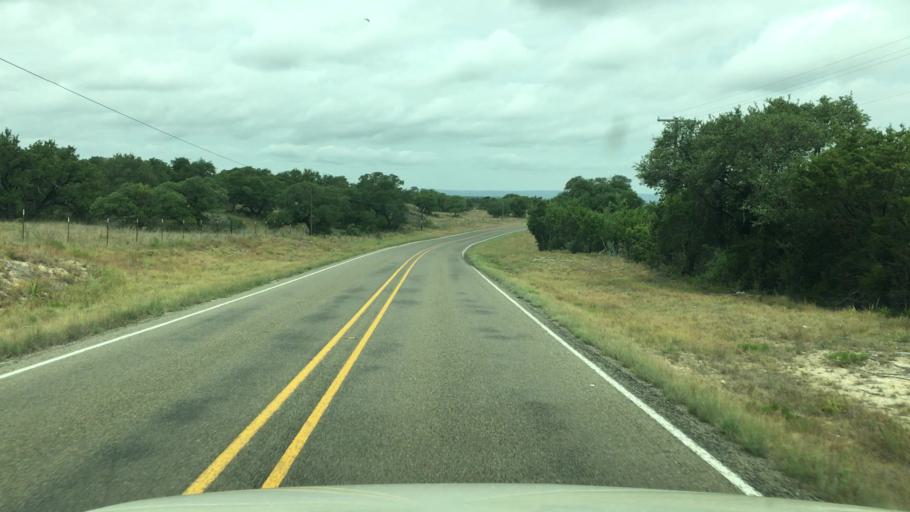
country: US
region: Texas
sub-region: Llano County
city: Horseshoe Bay
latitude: 30.4576
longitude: -98.3979
